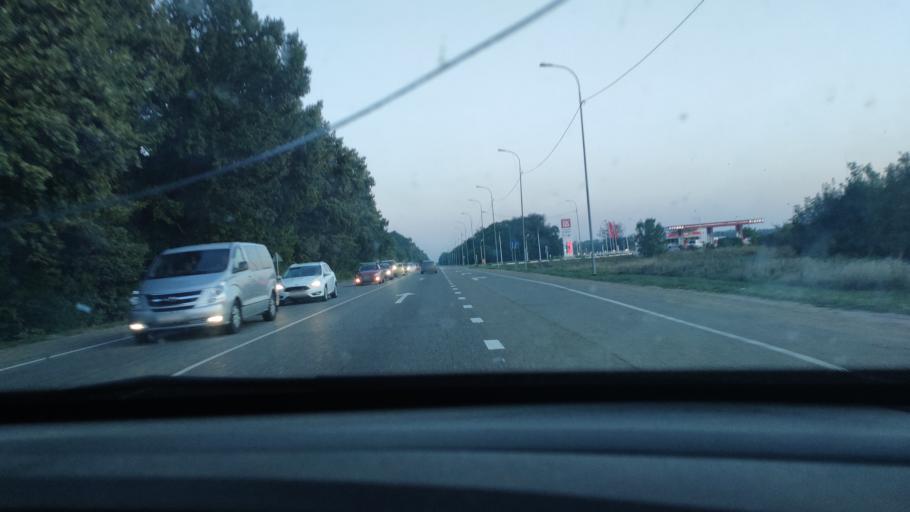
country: RU
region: Krasnodarskiy
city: Medvedovskaya
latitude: 45.4469
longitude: 38.9933
